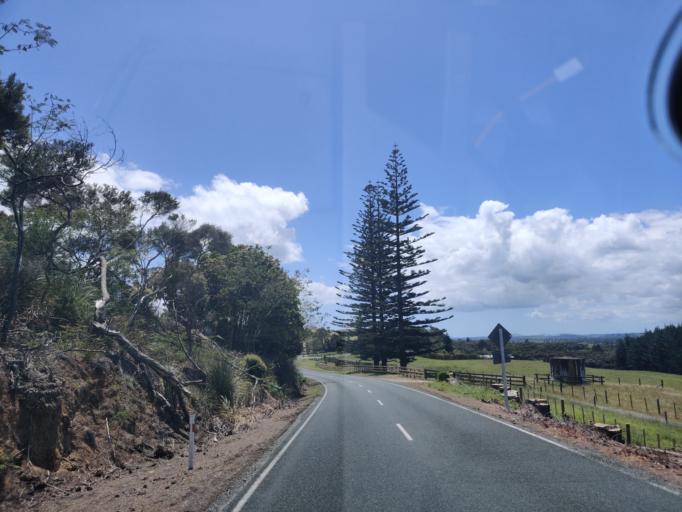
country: NZ
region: Northland
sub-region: Far North District
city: Kaitaia
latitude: -35.0254
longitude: 173.2080
